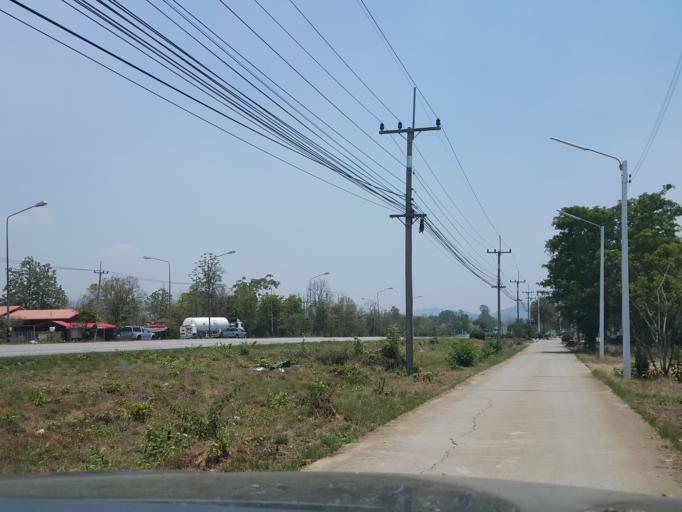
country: TH
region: Lampang
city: Thoen
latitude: 17.5445
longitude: 99.1963
